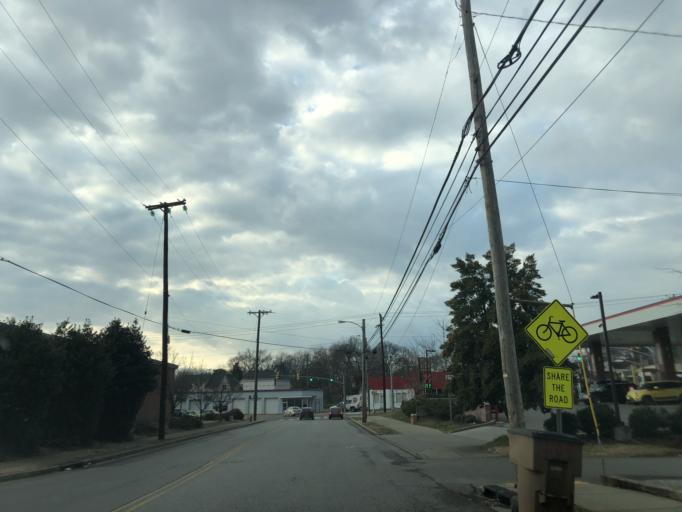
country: US
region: Tennessee
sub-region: Davidson County
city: Nashville
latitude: 36.1966
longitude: -86.7411
